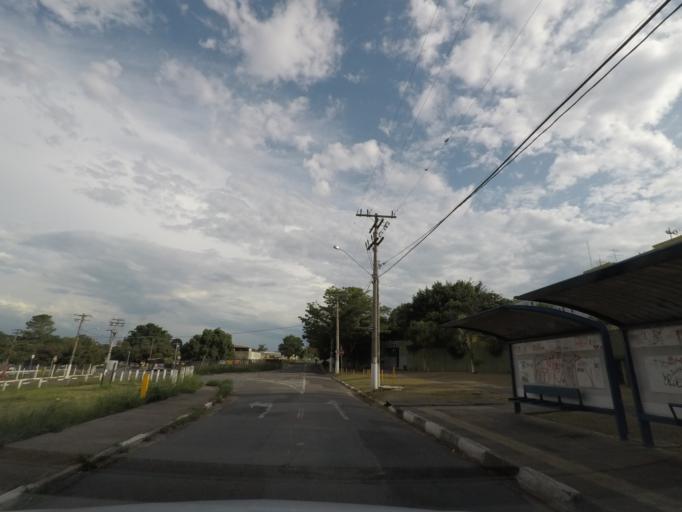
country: BR
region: Sao Paulo
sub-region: Campinas
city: Campinas
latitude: -22.9132
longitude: -47.1176
